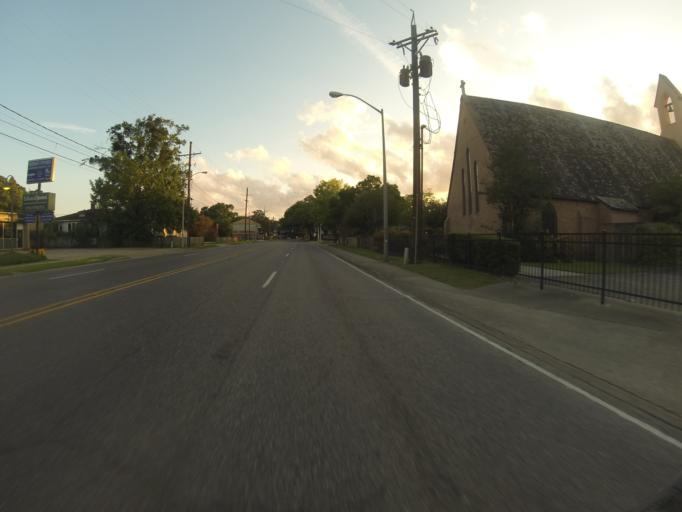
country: US
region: Louisiana
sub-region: Lafayette Parish
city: Lafayette
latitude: 30.2198
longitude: -92.0175
